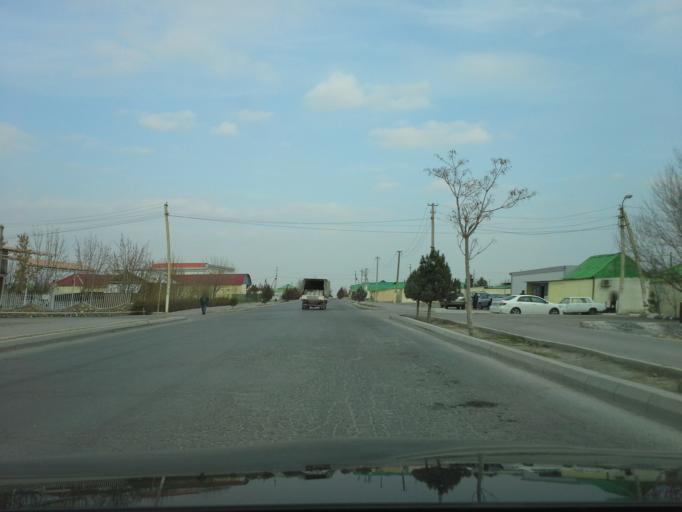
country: TM
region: Ahal
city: Abadan
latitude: 38.0324
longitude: 58.2498
